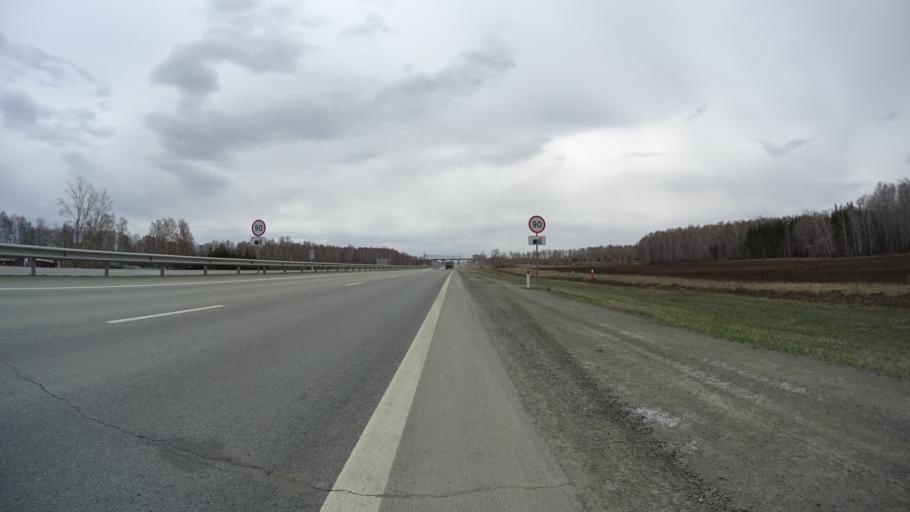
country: RU
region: Chelyabinsk
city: Yemanzhelinka
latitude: 54.8207
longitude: 61.3090
